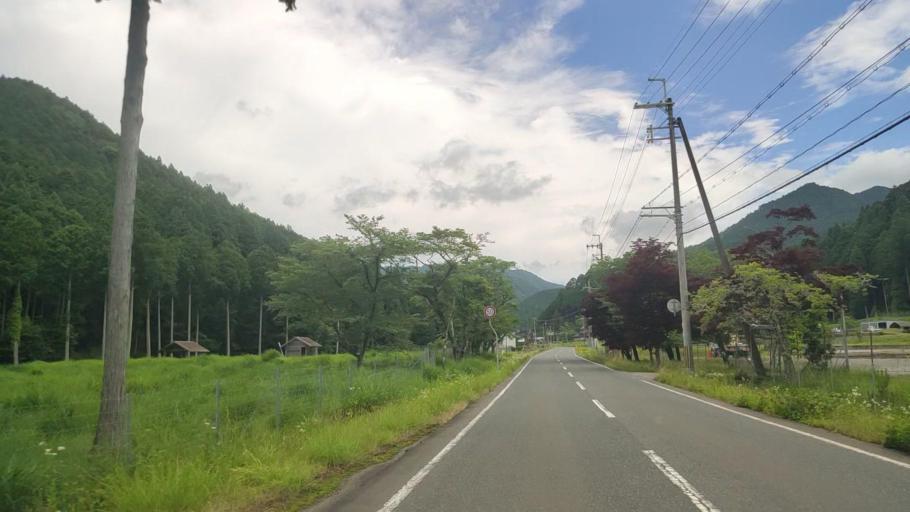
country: JP
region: Kyoto
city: Fukuchiyama
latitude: 35.1945
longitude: 134.9344
